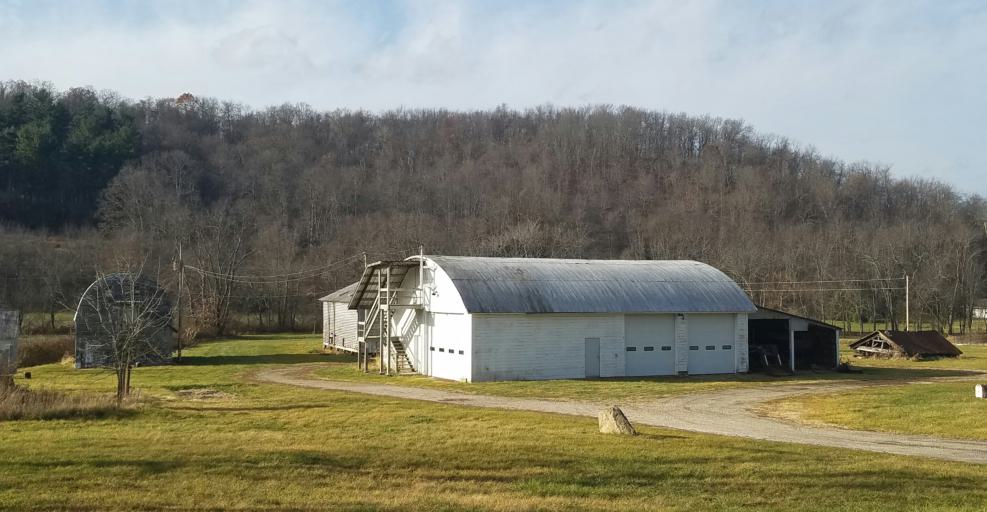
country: US
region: Ohio
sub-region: Knox County
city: Oak Hill
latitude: 40.4540
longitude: -82.0901
